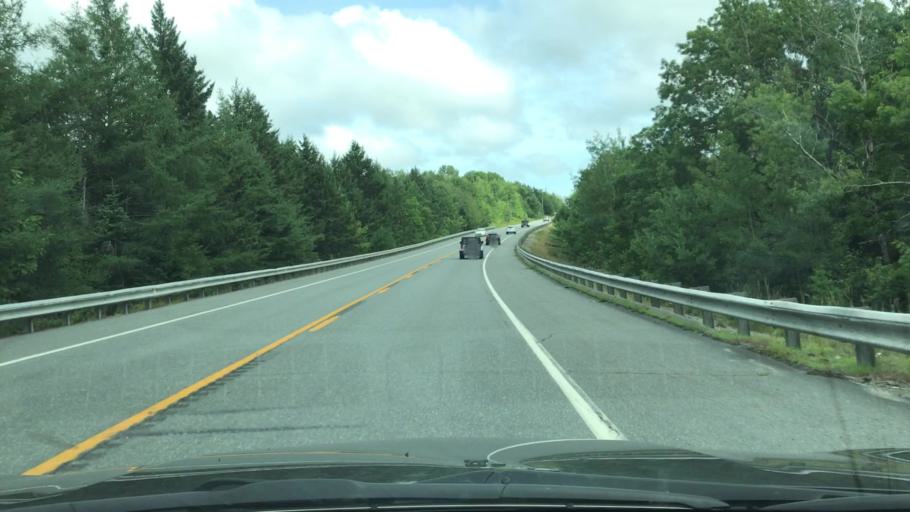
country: US
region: Maine
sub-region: Hancock County
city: Surry
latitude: 44.5563
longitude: -68.5434
